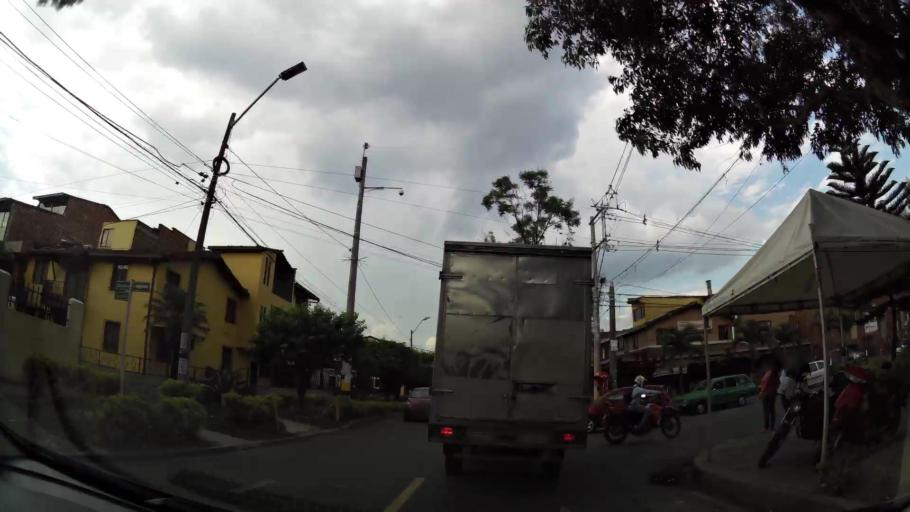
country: CO
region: Antioquia
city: Itagui
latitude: 6.2013
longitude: -75.5860
